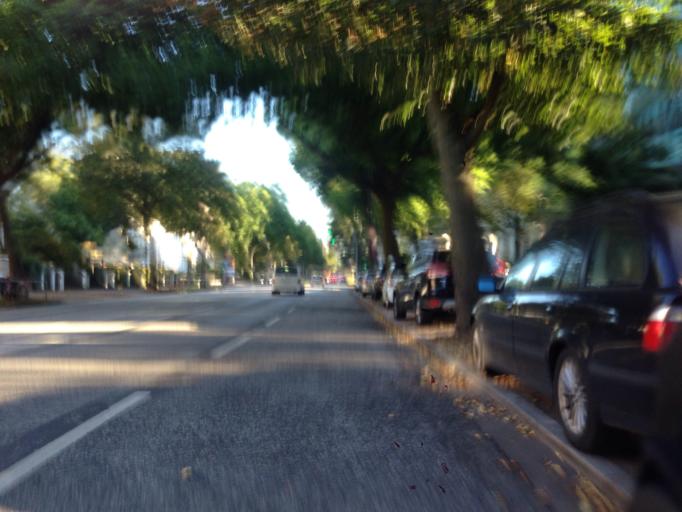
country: DE
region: Hamburg
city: Eimsbuettel
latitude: 53.5671
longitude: 9.9884
